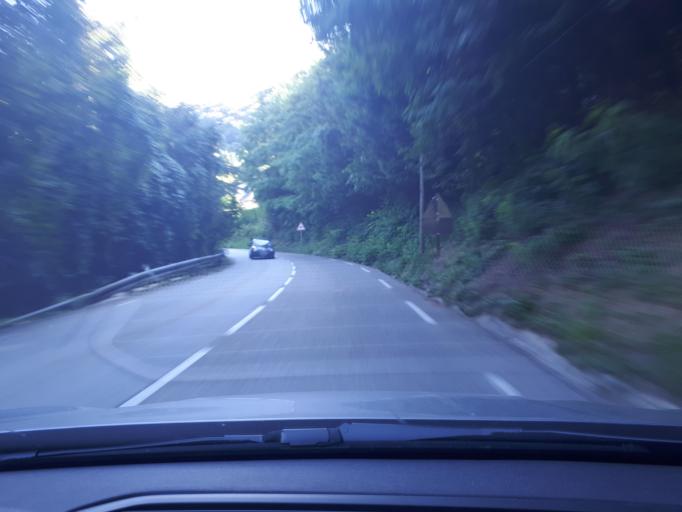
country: FR
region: Rhone-Alpes
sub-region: Departement de l'Isere
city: Seyssins
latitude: 45.1682
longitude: 5.6785
